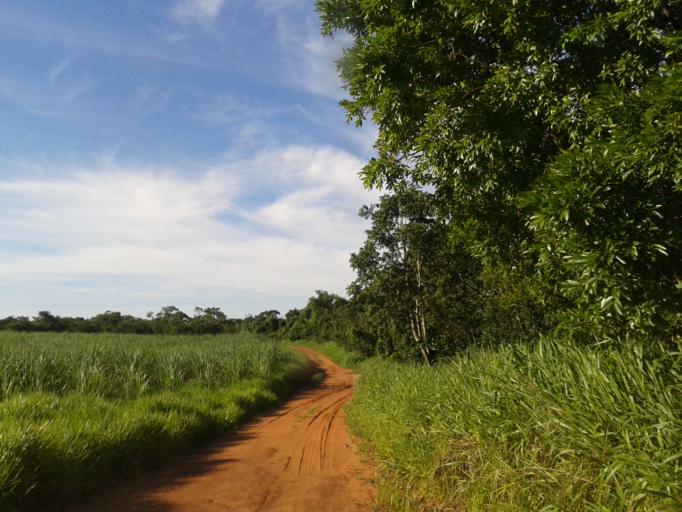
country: BR
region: Minas Gerais
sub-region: Santa Vitoria
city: Santa Vitoria
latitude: -19.1151
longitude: -49.9914
